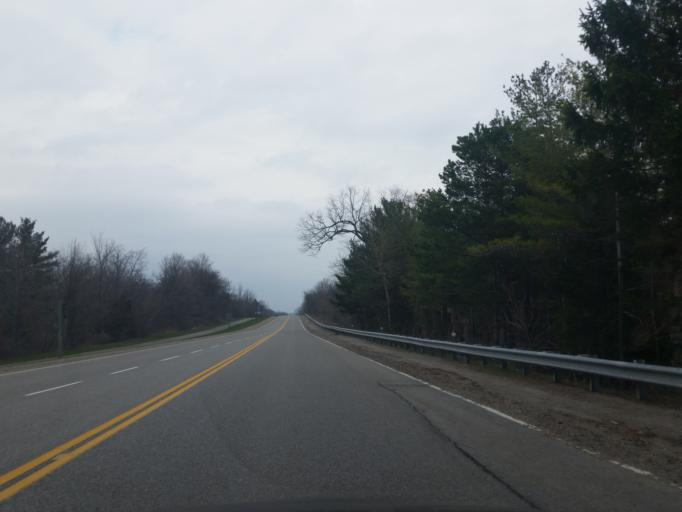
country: US
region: New York
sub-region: Jefferson County
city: Alexandria Bay
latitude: 44.3850
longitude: -75.9316
